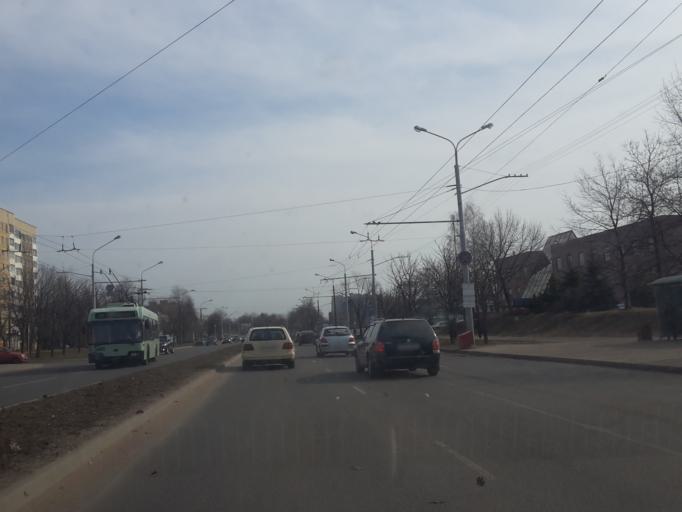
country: BY
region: Minsk
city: Novoye Medvezhino
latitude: 53.8935
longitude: 27.4850
